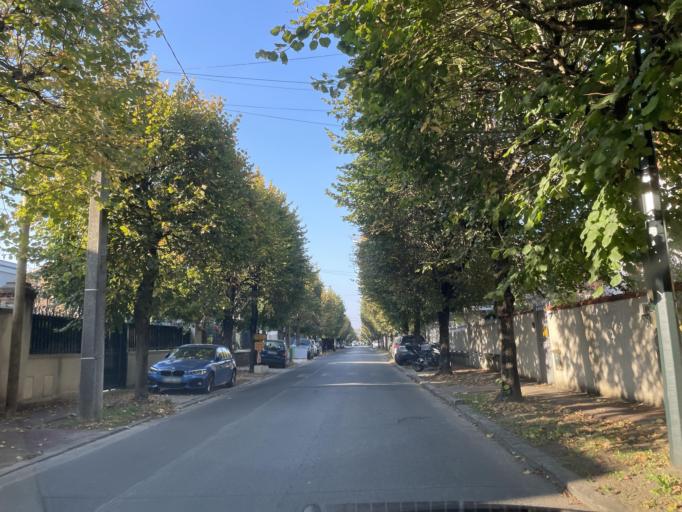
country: FR
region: Ile-de-France
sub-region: Departement du Val-de-Marne
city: Chennevieres-sur-Marne
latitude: 48.8012
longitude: 2.5187
